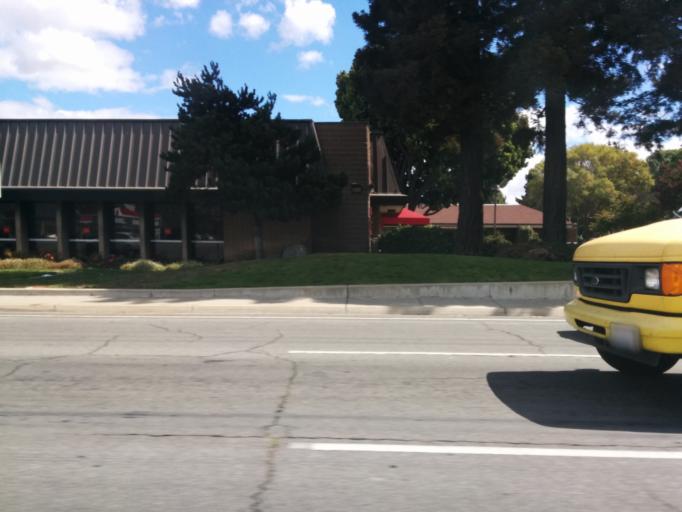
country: US
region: California
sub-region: Santa Clara County
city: Sunnyvale
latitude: 37.3796
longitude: -121.9958
